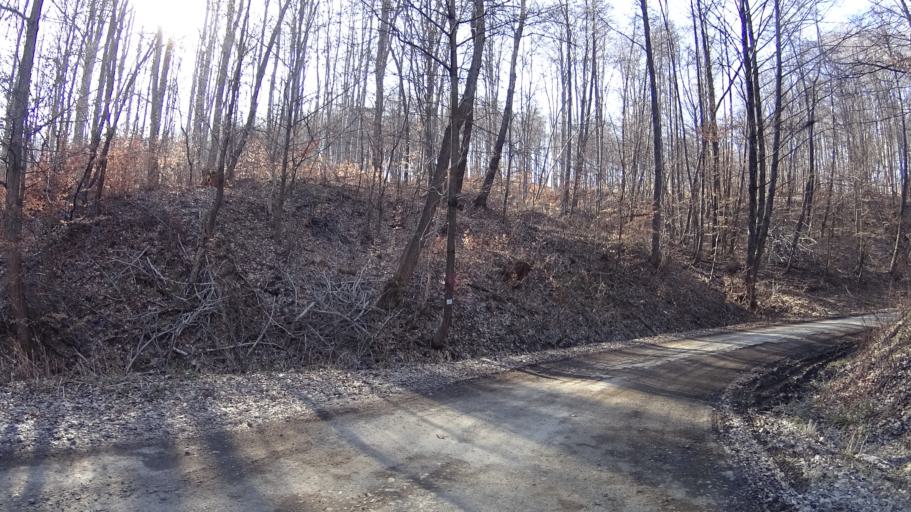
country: HU
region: Heves
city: Paradsasvar
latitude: 47.9367
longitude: 19.9082
